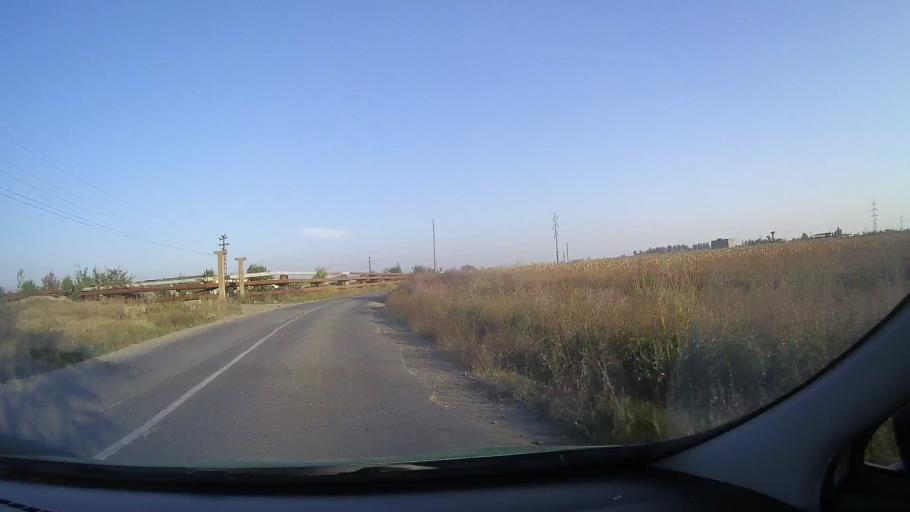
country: RO
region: Bihor
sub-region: Comuna Bors
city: Santion
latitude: 47.1110
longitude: 21.8628
